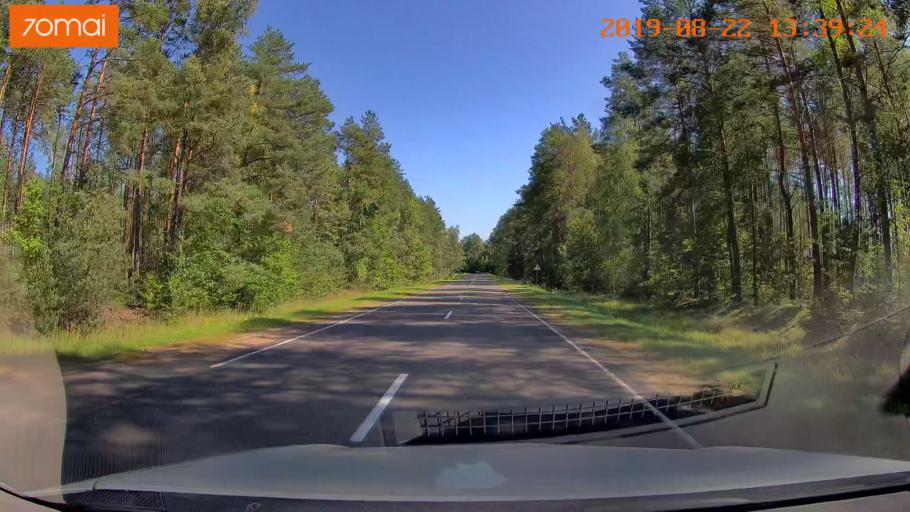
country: BY
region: Minsk
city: Staryya Darohi
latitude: 53.2276
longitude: 28.3485
